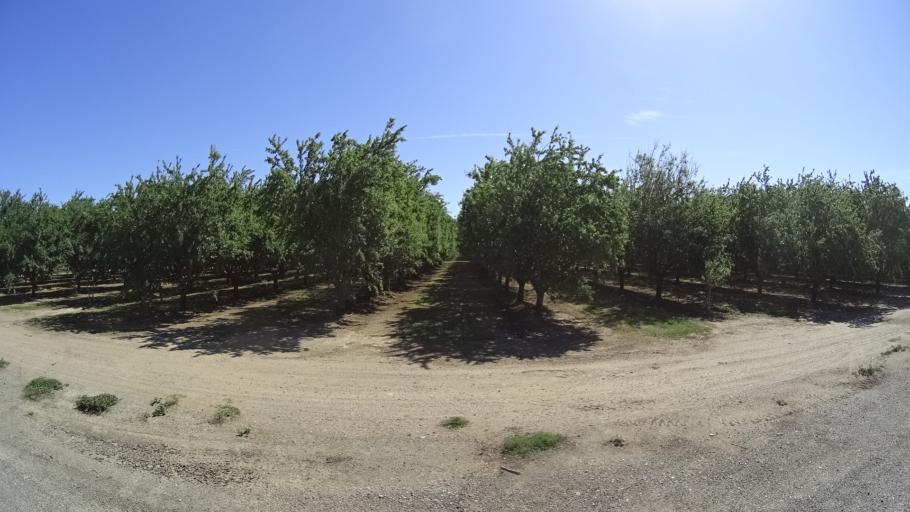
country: US
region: California
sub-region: Glenn County
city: Hamilton City
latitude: 39.6989
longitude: -122.1033
